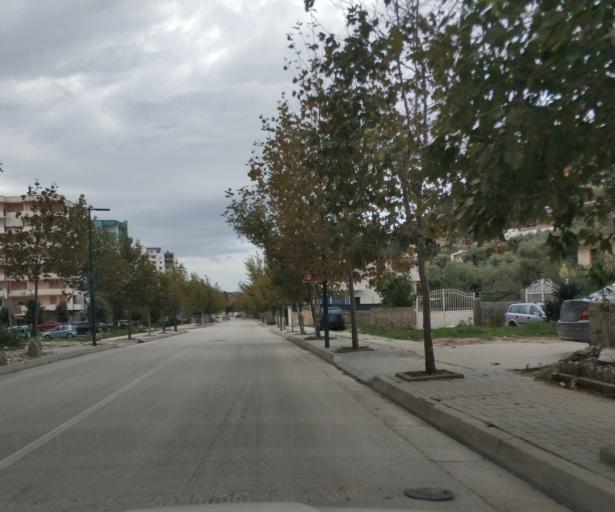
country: AL
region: Vlore
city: Vlore
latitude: 40.4426
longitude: 19.4973
